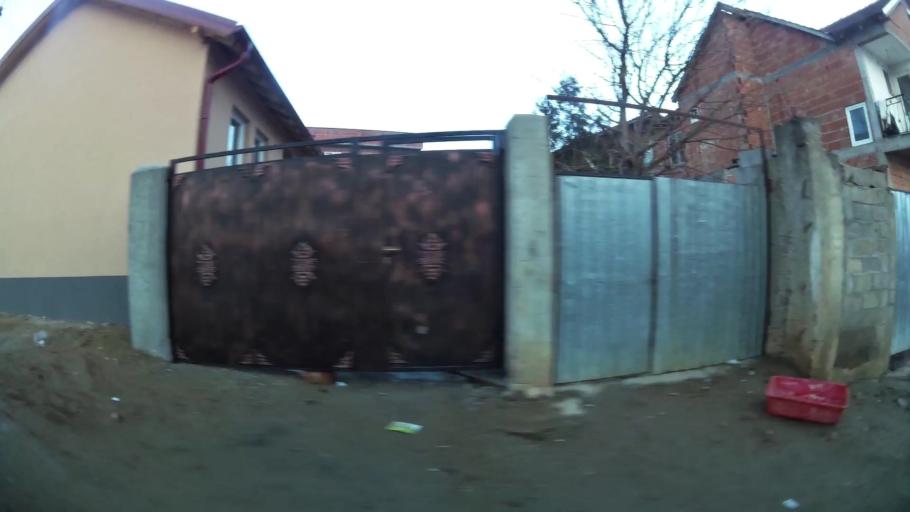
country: MK
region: Aracinovo
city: Arachinovo
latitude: 42.0300
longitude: 21.5590
